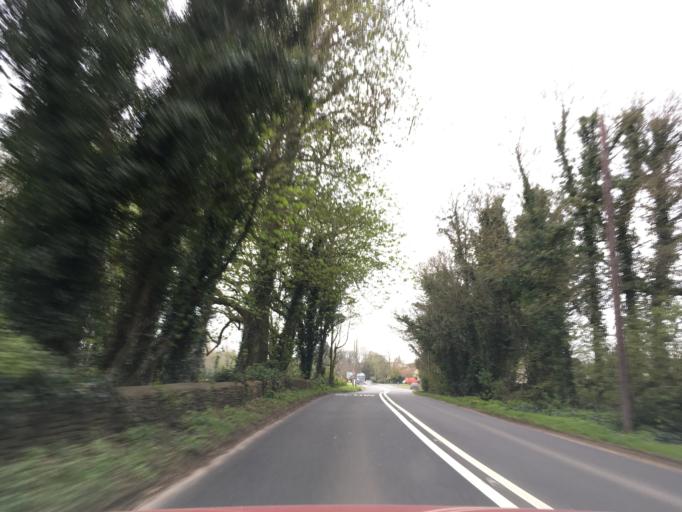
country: GB
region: England
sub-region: Gloucestershire
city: Coates
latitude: 51.6779
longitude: -2.0161
